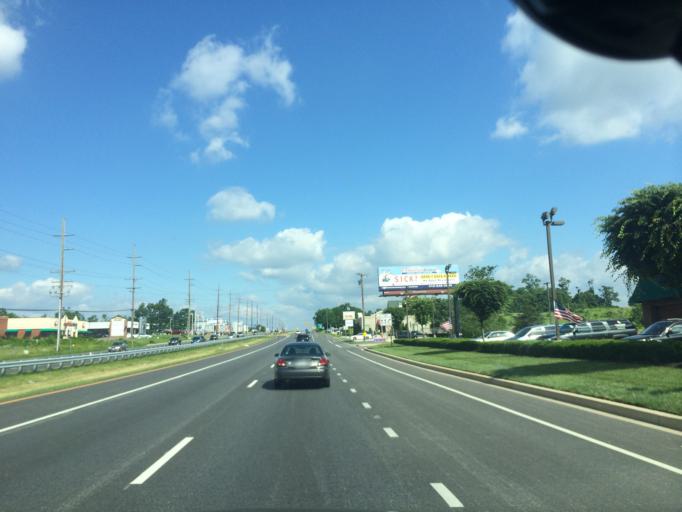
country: US
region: Maryland
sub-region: Carroll County
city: Westminster
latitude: 39.5556
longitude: -76.9595
